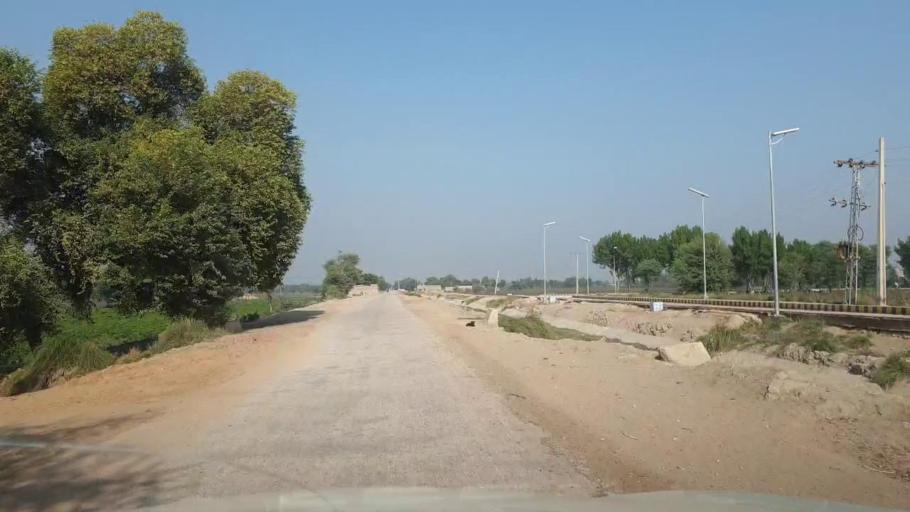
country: PK
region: Sindh
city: Bhan
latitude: 26.5381
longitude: 67.7754
